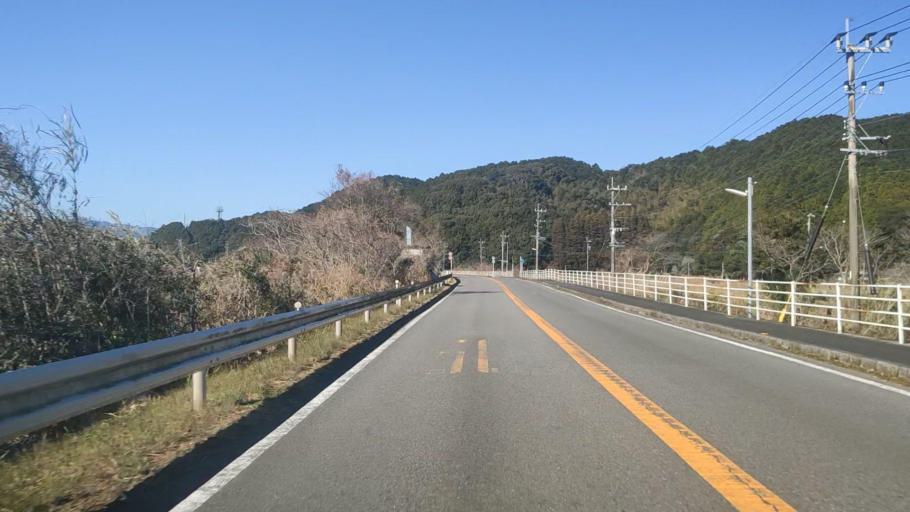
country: JP
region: Oita
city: Saiki
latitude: 32.9386
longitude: 131.9152
